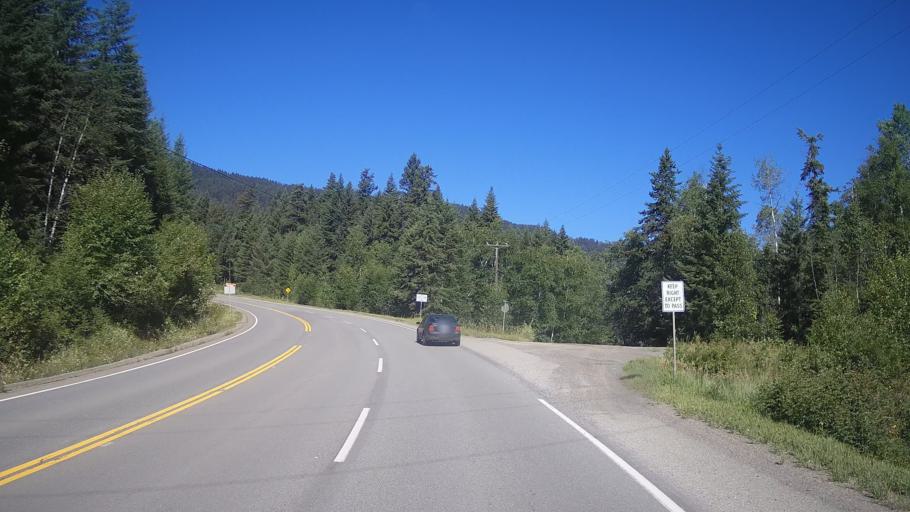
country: CA
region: British Columbia
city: Kamloops
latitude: 51.4666
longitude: -120.2352
